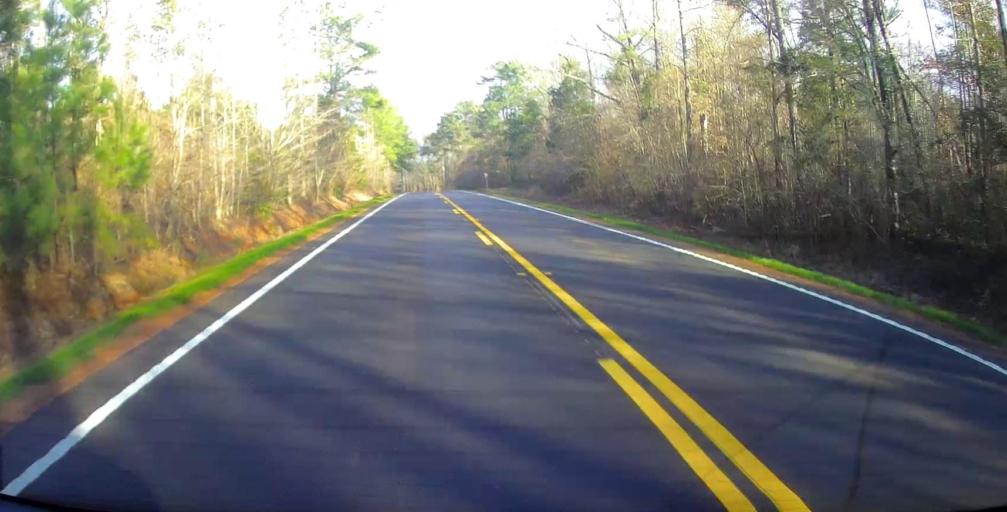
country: US
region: Georgia
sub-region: Harris County
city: Hamilton
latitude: 32.7483
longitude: -84.9163
